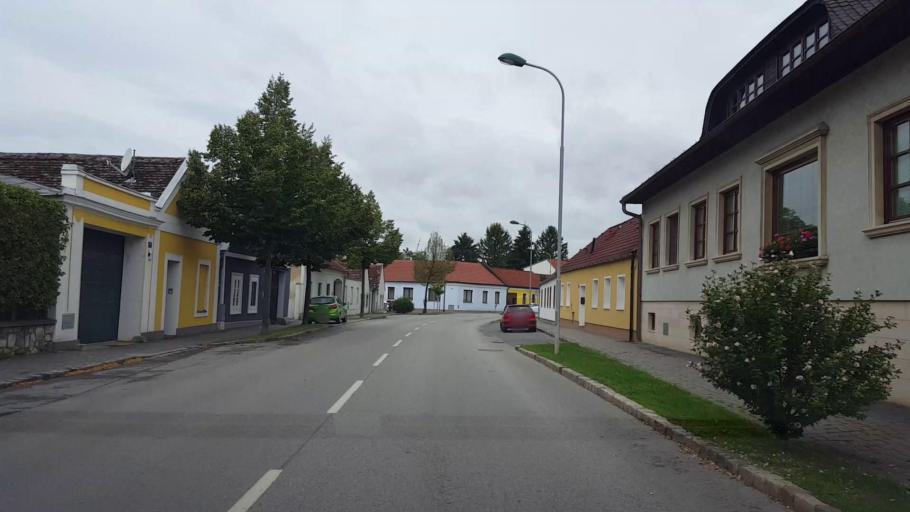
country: AT
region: Lower Austria
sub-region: Politischer Bezirk Bruck an der Leitha
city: Bruck an der Leitha
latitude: 48.0133
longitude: 16.7211
